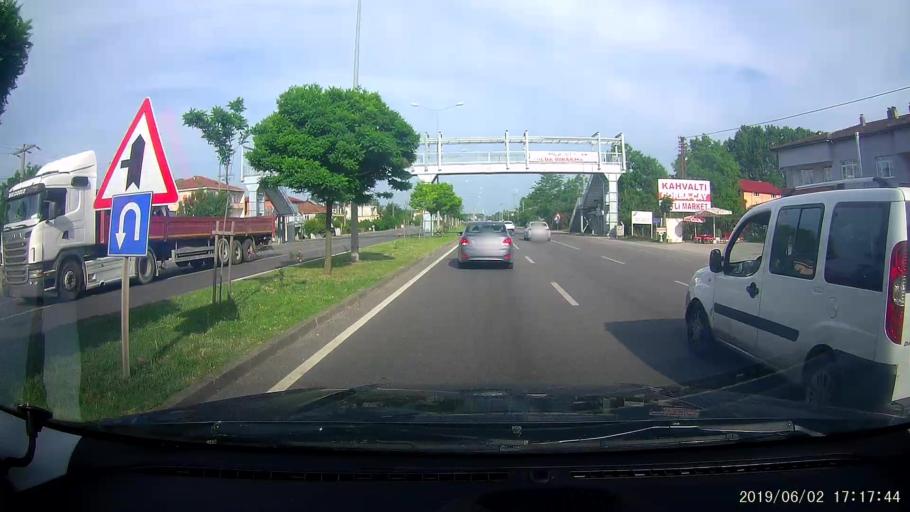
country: TR
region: Samsun
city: Dikbiyik
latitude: 41.2273
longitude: 36.5860
